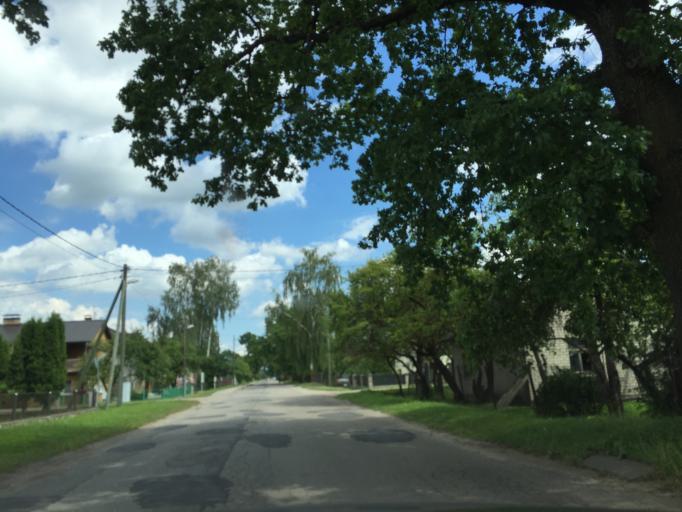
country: LV
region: Jelgava
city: Jelgava
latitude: 56.6286
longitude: 23.7084
